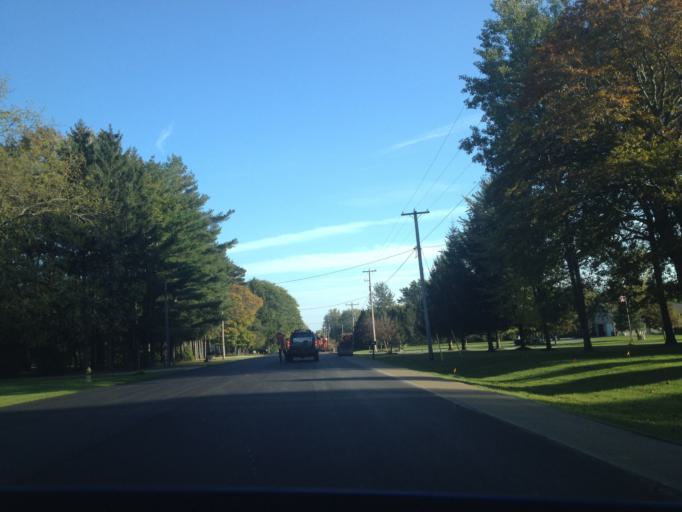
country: CA
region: Ontario
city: Delaware
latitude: 42.5758
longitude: -81.5724
